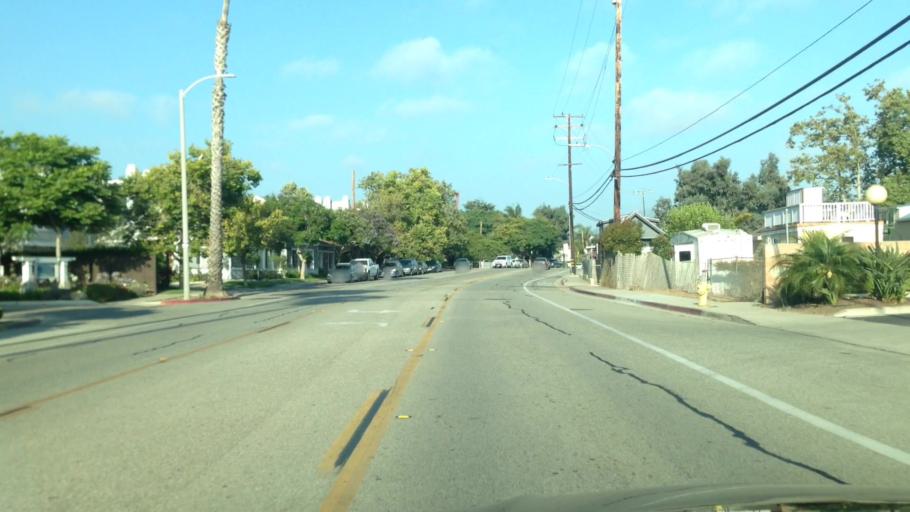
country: US
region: California
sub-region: Santa Barbara County
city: Carpinteria
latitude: 34.4016
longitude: -119.5233
